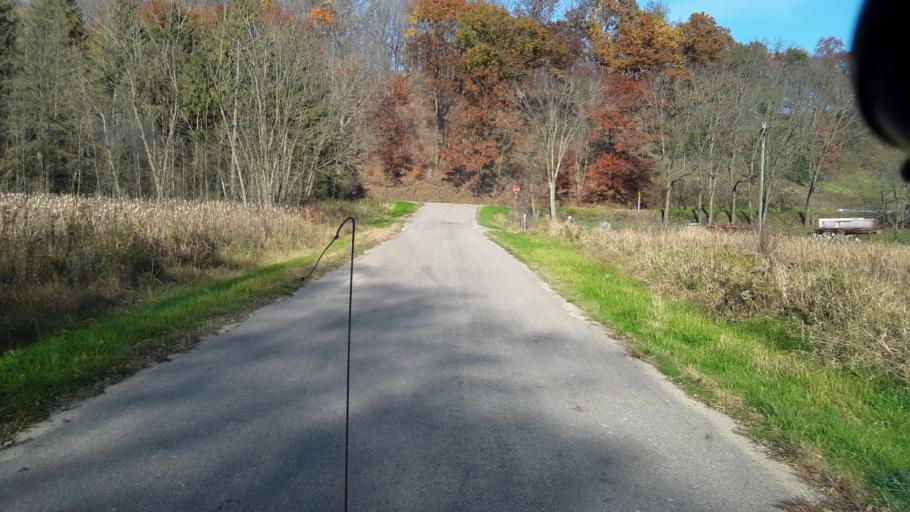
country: US
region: Wisconsin
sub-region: Vernon County
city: Hillsboro
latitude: 43.6605
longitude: -90.4443
